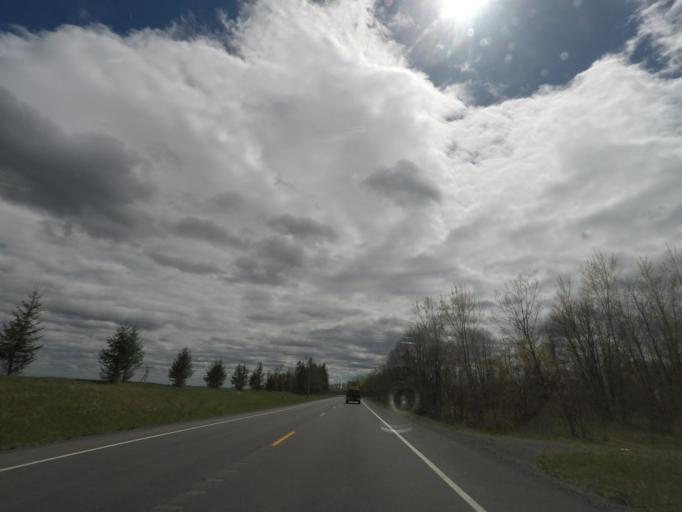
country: US
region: New York
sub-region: Albany County
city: Ravena
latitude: 42.4847
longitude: -73.7939
